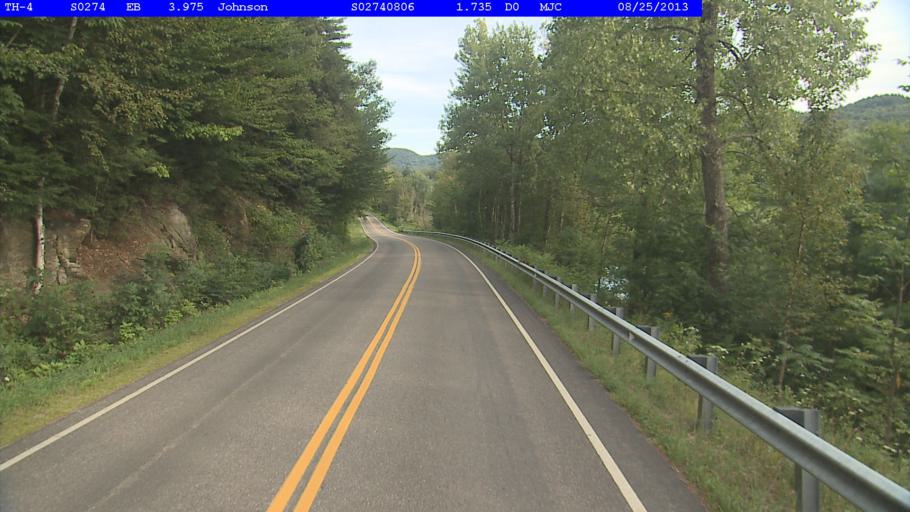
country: US
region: Vermont
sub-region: Lamoille County
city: Johnson
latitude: 44.6468
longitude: -72.7213
